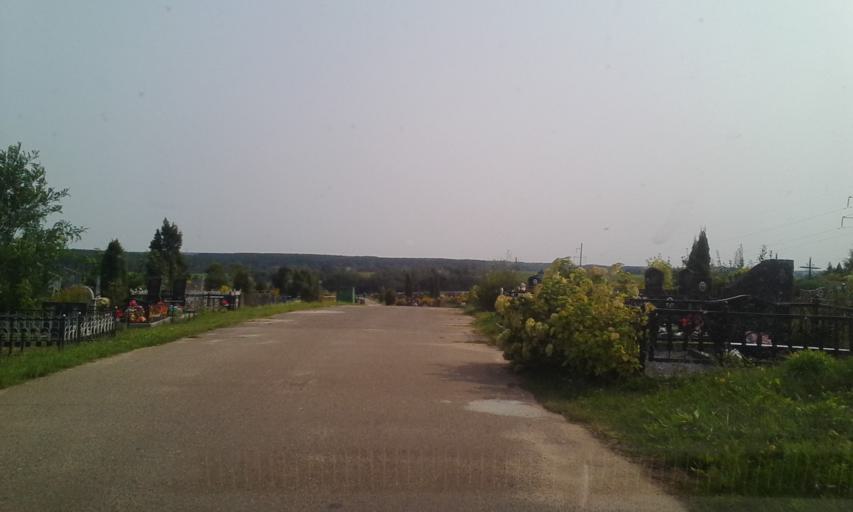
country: BY
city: Michanovichi
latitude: 53.7663
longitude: 27.6994
